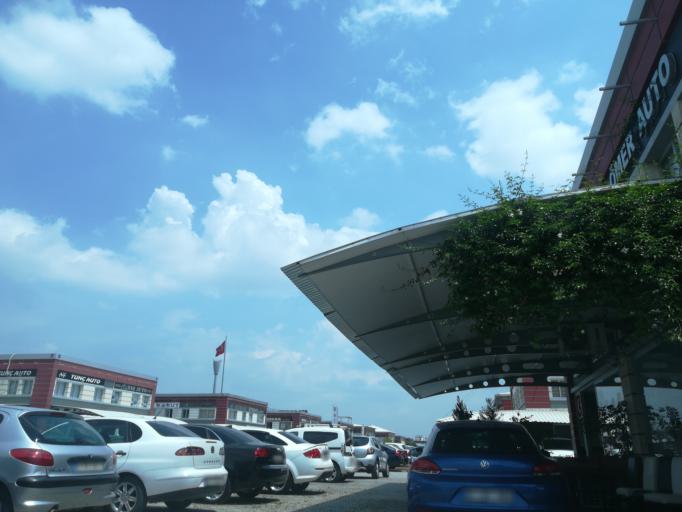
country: TR
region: Adana
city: Seyhan
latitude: 37.0016
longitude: 35.2432
